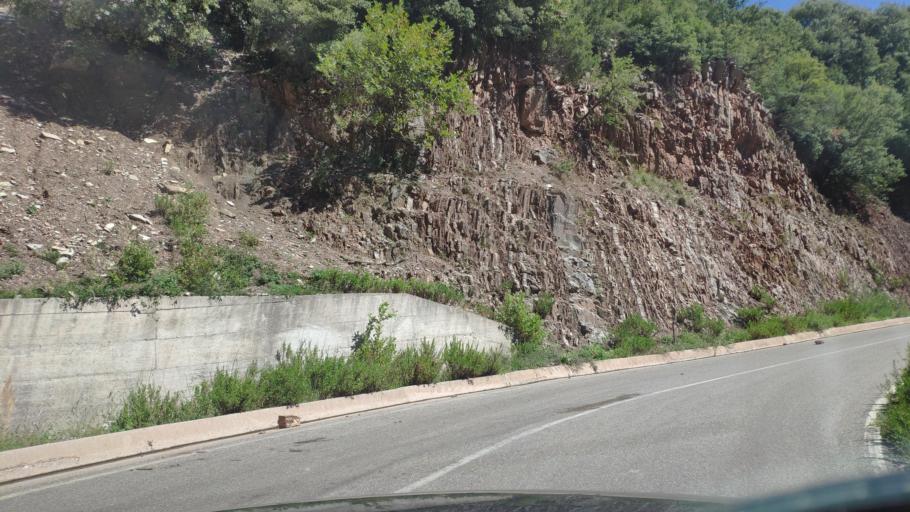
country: GR
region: Central Greece
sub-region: Nomos Evrytanias
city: Kerasochori
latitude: 39.0806
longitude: 21.5952
